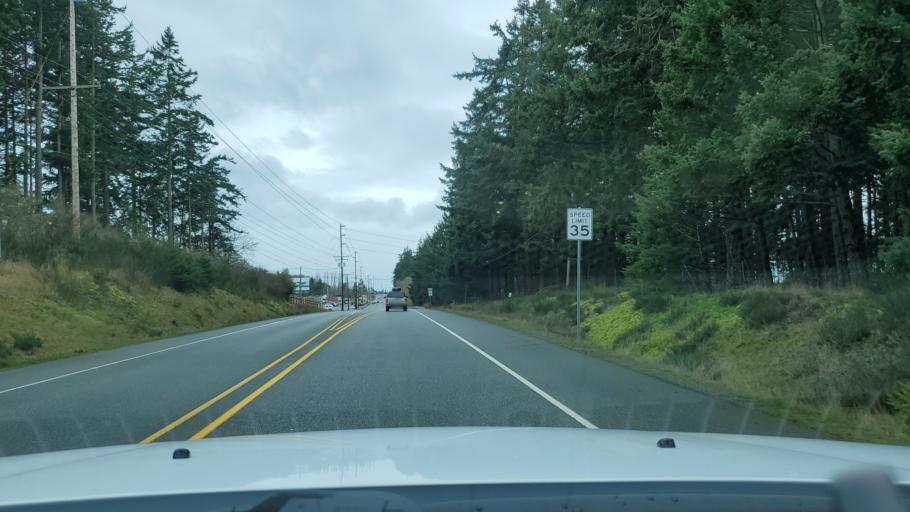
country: US
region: Washington
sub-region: Island County
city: Ault Field
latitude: 48.3259
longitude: -122.6624
